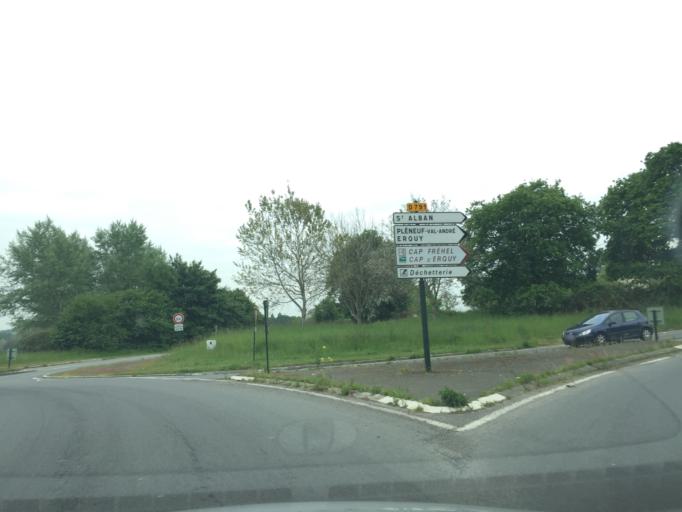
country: FR
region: Brittany
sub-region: Departement des Cotes-d'Armor
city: Lamballe
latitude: 48.4811
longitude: -2.5138
